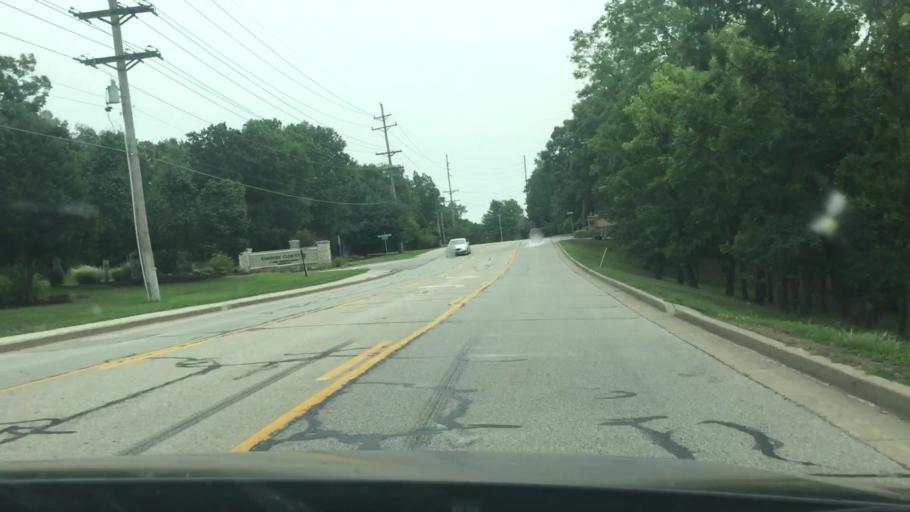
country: US
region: Missouri
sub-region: Camden County
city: Four Seasons
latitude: 38.1908
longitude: -92.6986
